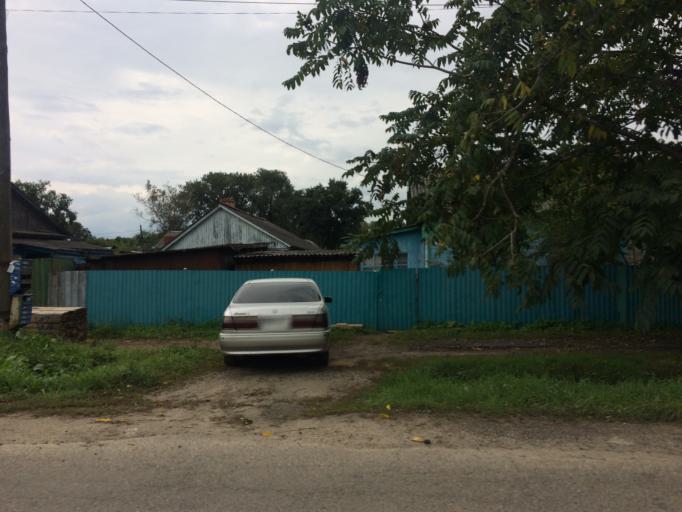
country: RU
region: Primorskiy
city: Dal'nerechensk
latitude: 45.9296
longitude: 133.7624
